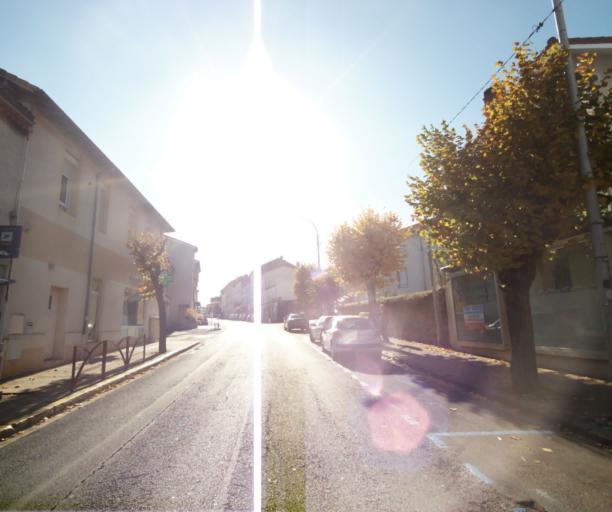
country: FR
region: Auvergne
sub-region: Departement du Puy-de-Dome
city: Ceyrat
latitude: 45.7319
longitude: 3.0636
